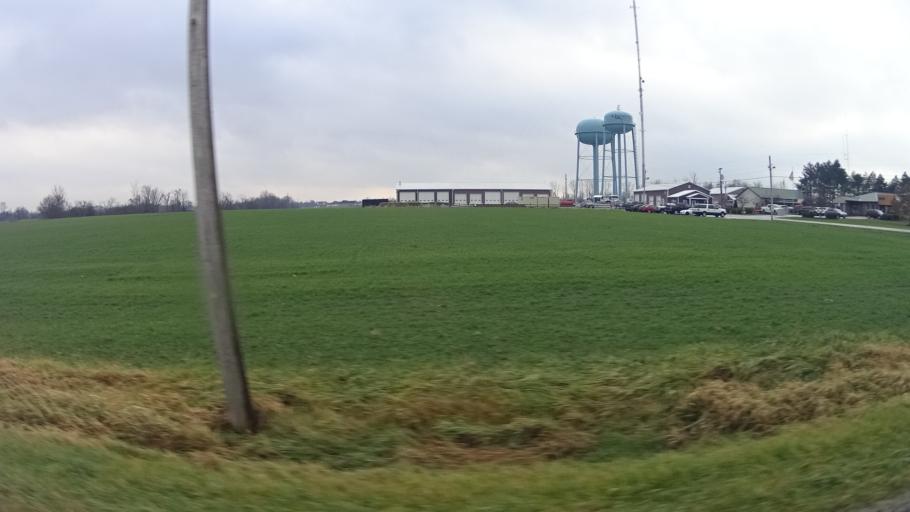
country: US
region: Ohio
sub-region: Lorain County
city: Lagrange
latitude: 41.2372
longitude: -82.1472
